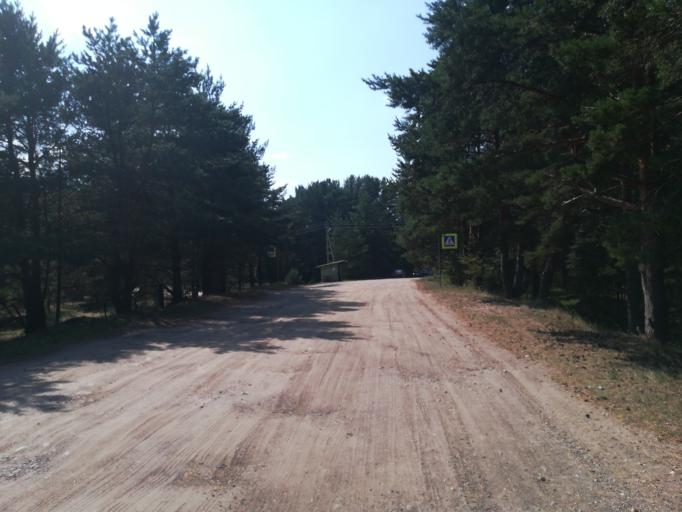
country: RU
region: Leningrad
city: Ust'-Luga
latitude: 59.7742
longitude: 28.1301
